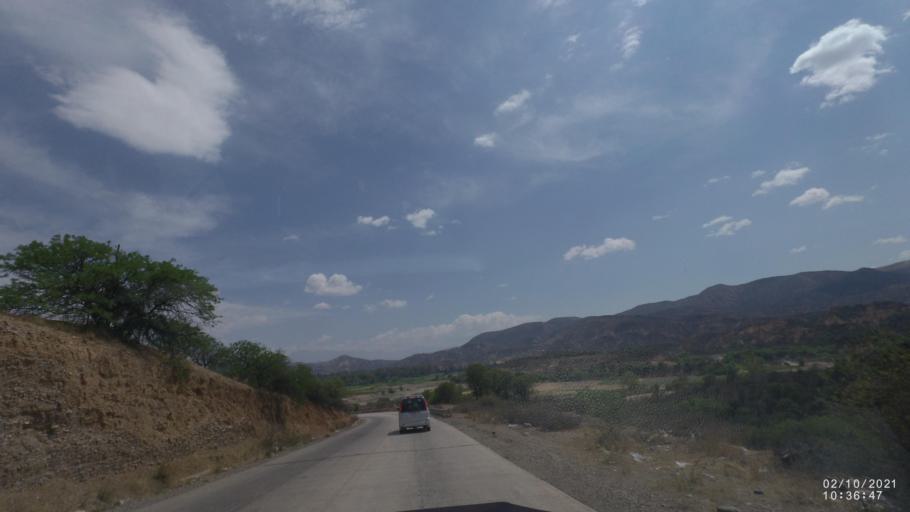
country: BO
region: Cochabamba
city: Capinota
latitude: -17.6467
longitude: -66.2589
